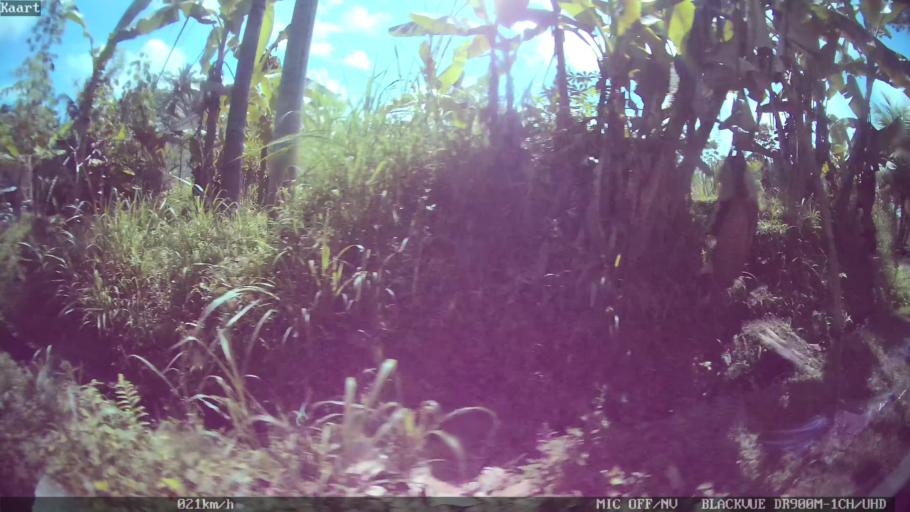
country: ID
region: Bali
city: Banjar Kelodan
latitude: -8.5121
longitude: 115.3353
